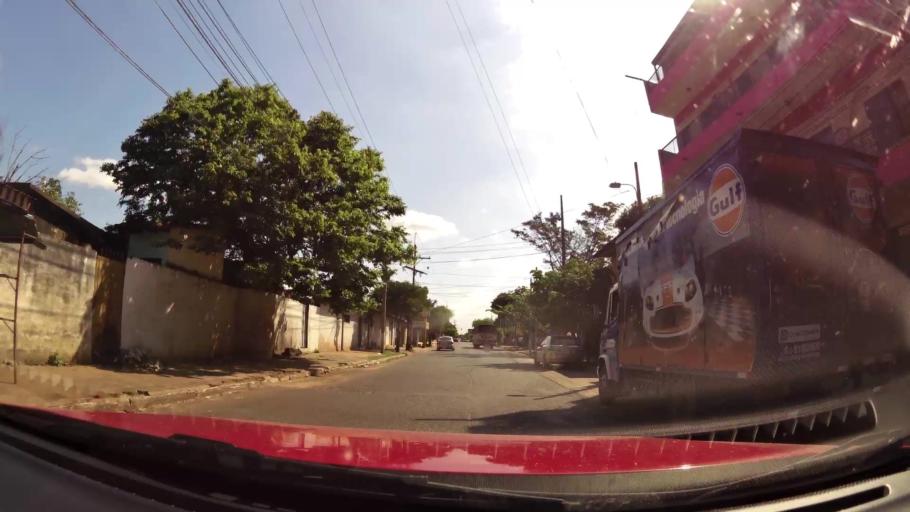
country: PY
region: Central
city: San Lorenzo
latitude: -25.3457
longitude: -57.5024
